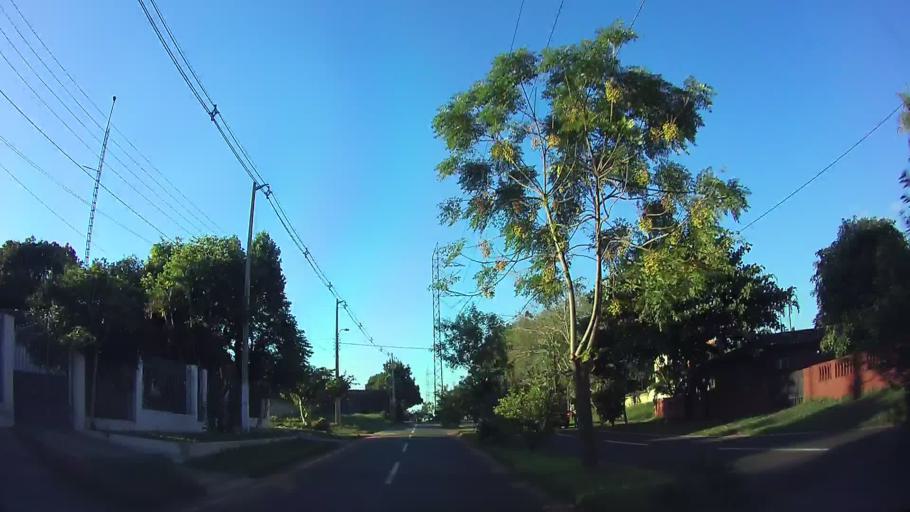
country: PY
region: Central
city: San Lorenzo
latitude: -25.2784
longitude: -57.4643
